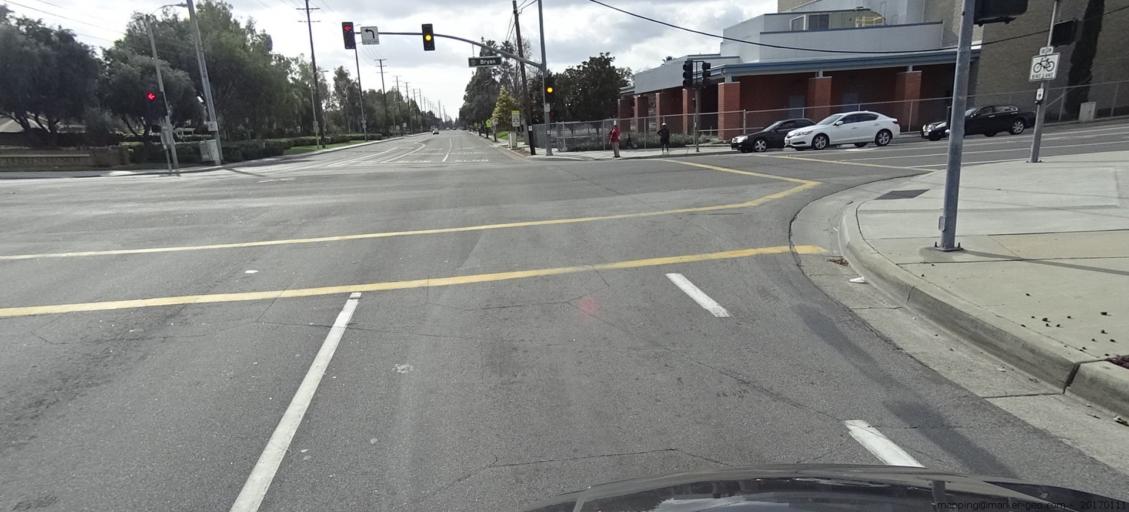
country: US
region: California
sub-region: Orange County
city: Tustin
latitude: 33.7347
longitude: -117.8030
